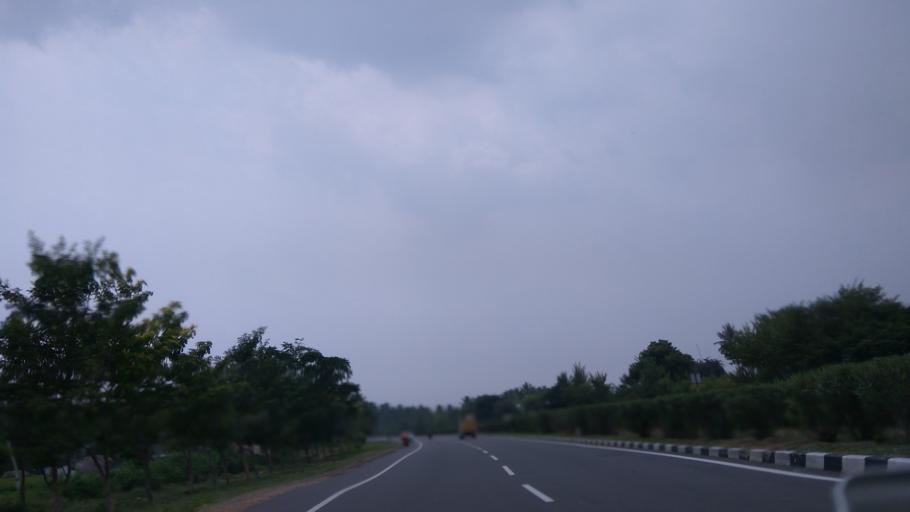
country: IN
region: Tamil Nadu
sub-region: Dharmapuri
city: Dharmapuri
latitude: 12.2013
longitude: 78.1831
